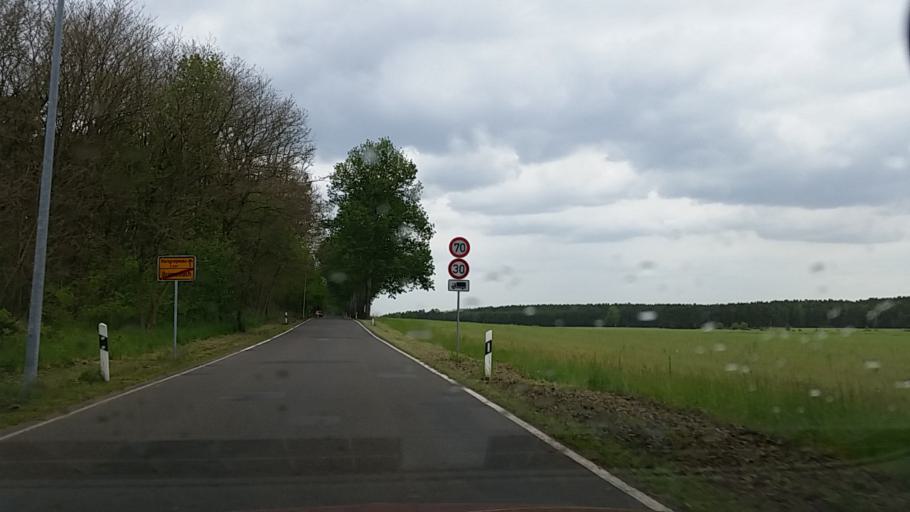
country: DE
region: Brandenburg
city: Rauen
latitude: 52.3153
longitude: 13.9639
